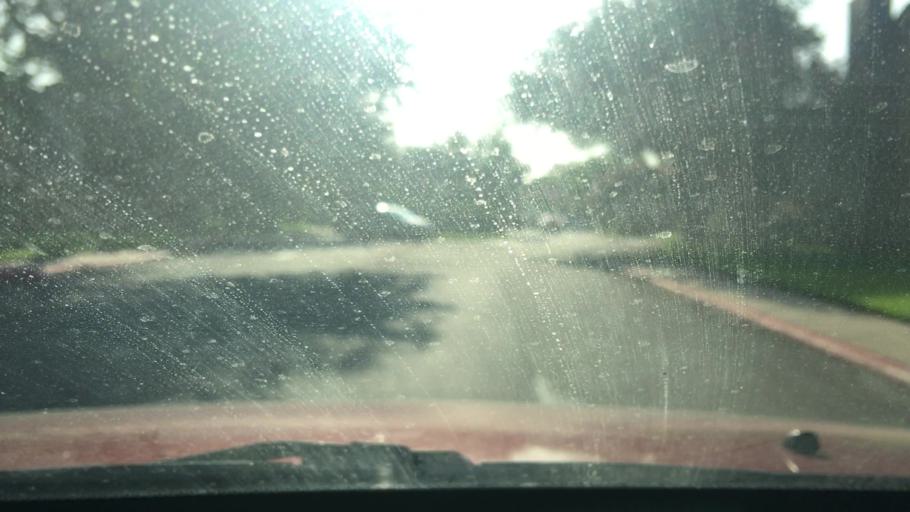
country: US
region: Texas
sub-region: Dallas County
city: Addison
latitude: 32.9571
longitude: -96.8055
